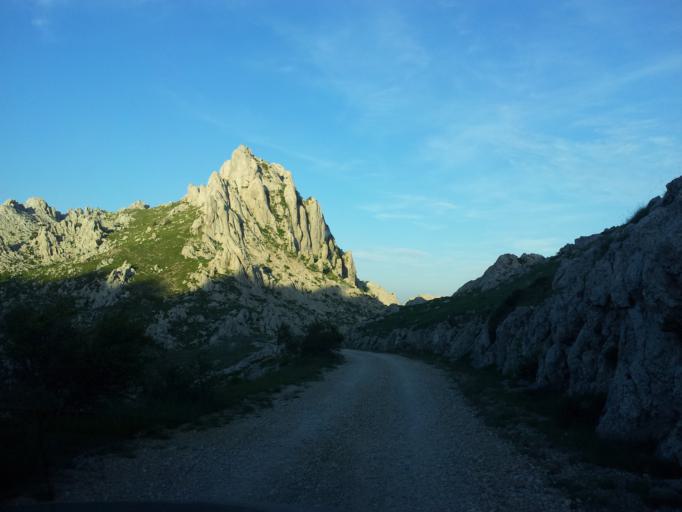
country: HR
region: Zadarska
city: Obrovac
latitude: 44.2644
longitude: 15.6426
